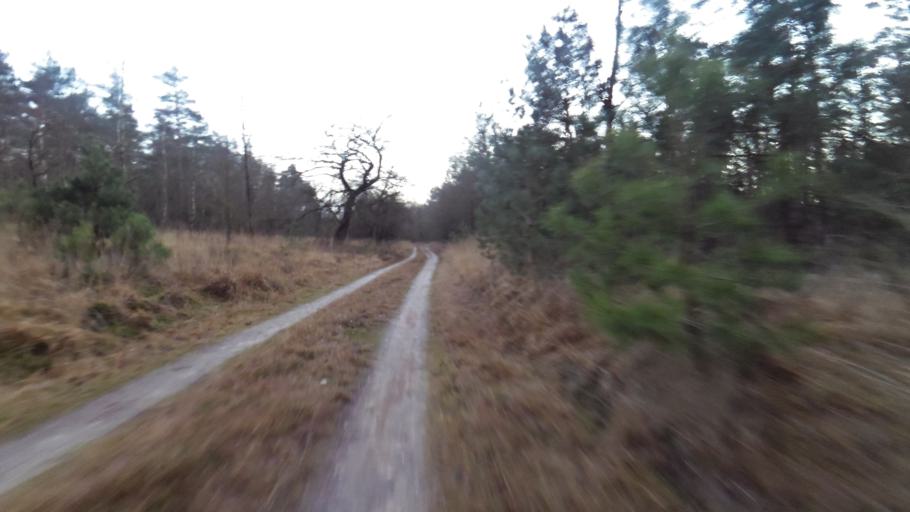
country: NL
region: Gelderland
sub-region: Gemeente Apeldoorn
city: Uddel
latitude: 52.2760
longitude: 5.8485
